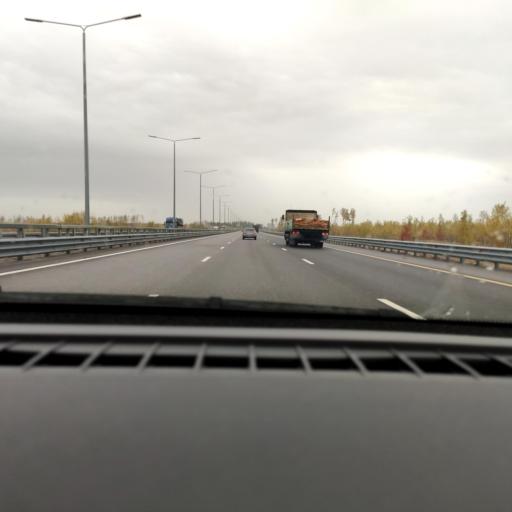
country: RU
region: Voronezj
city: Somovo
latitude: 51.7698
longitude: 39.3028
